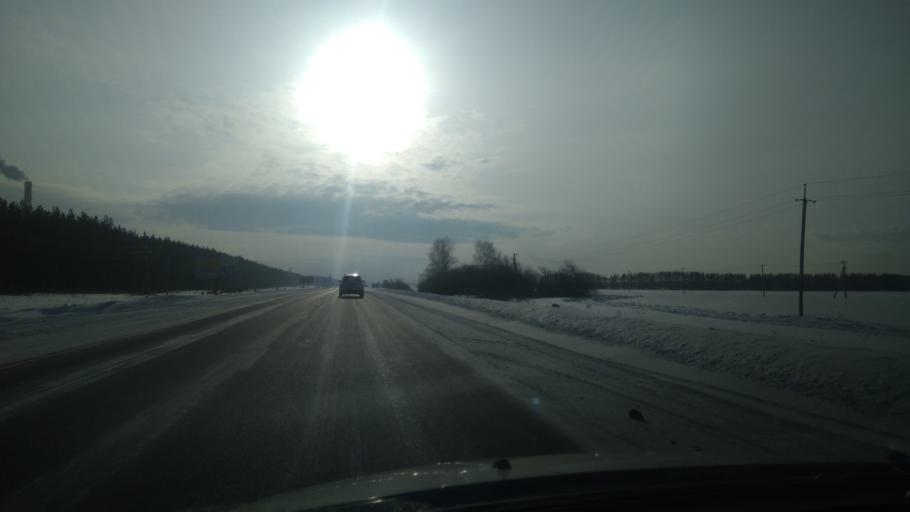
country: RU
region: Sverdlovsk
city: Sukhoy Log
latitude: 56.8737
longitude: 62.0460
